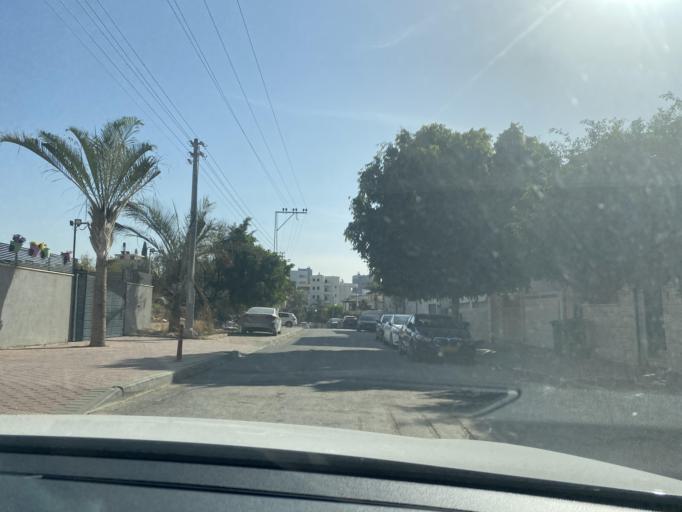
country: IL
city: Oranit
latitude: 32.1325
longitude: 34.9746
